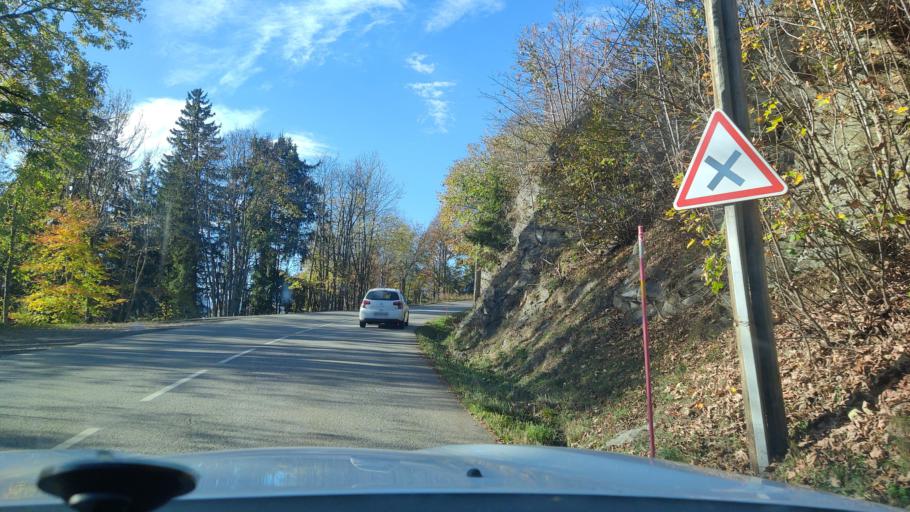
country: FR
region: Rhone-Alpes
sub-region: Departement de la Savoie
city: Beaufort
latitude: 45.7453
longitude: 6.5703
